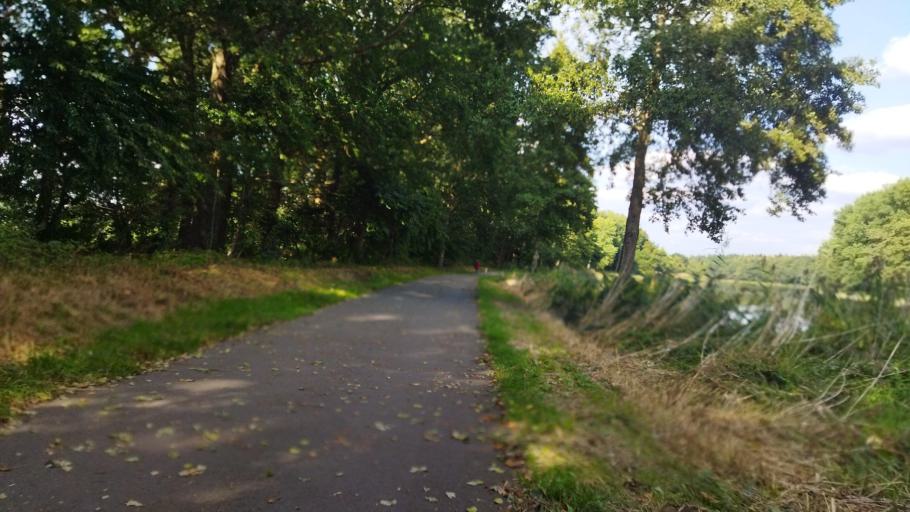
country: DE
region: Lower Saxony
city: Walchum
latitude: 52.9338
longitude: 7.2894
